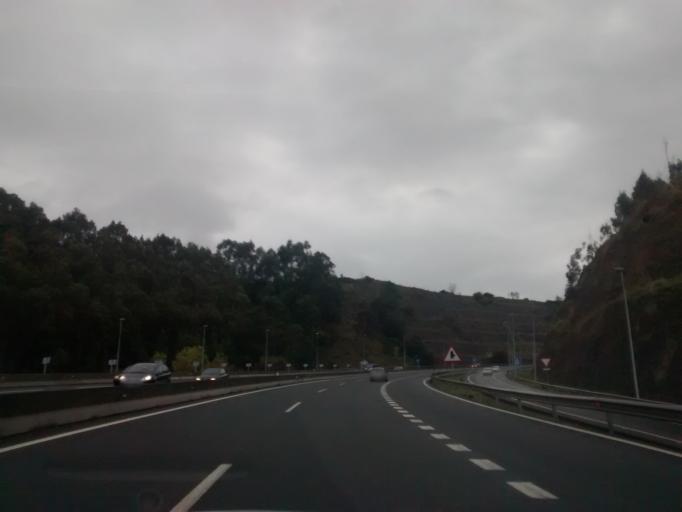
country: ES
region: Cantabria
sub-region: Provincia de Cantabria
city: Castro-Urdiales
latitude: 43.3642
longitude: -3.2181
